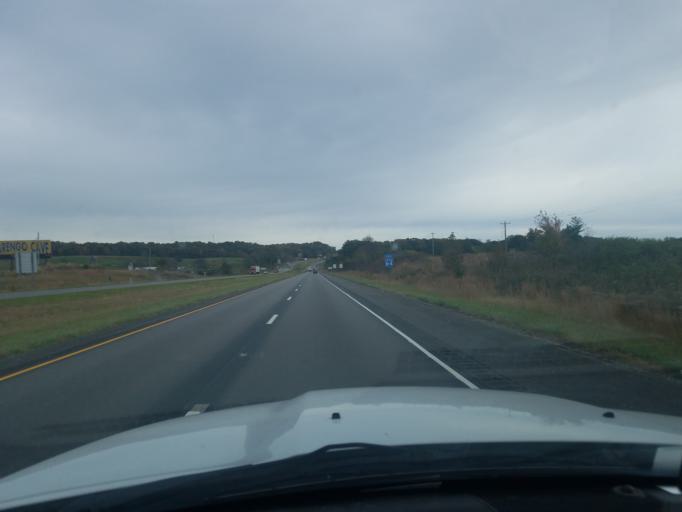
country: US
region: Indiana
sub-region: Dubois County
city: Ferdinand
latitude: 38.2052
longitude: -86.8558
